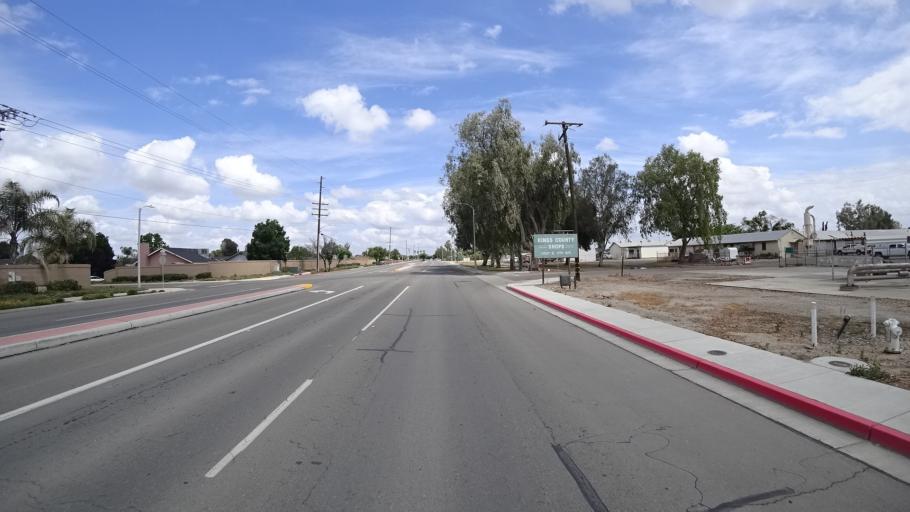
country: US
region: California
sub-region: Kings County
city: Home Garden
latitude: 36.3005
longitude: -119.6548
